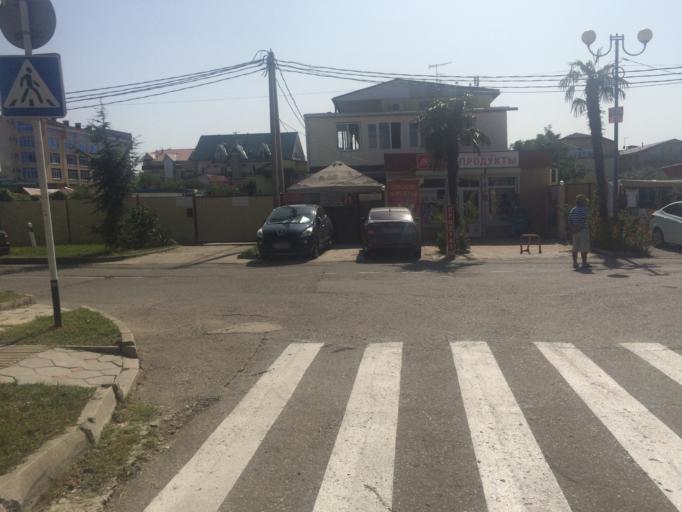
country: RU
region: Krasnodarskiy
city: Adler
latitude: 43.3978
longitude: 39.9717
